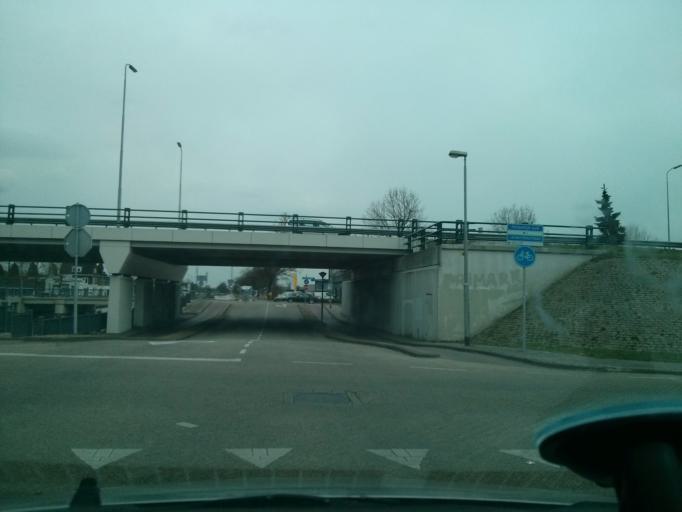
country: NL
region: North Brabant
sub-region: Gemeente Eindhoven
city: Lakerlopen
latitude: 51.4349
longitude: 5.5034
